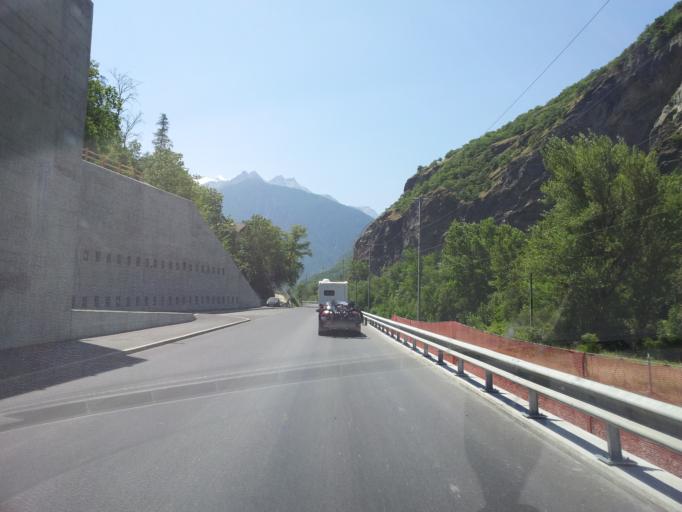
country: CH
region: Valais
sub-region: Visp District
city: Visp
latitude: 46.2763
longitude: 7.8826
